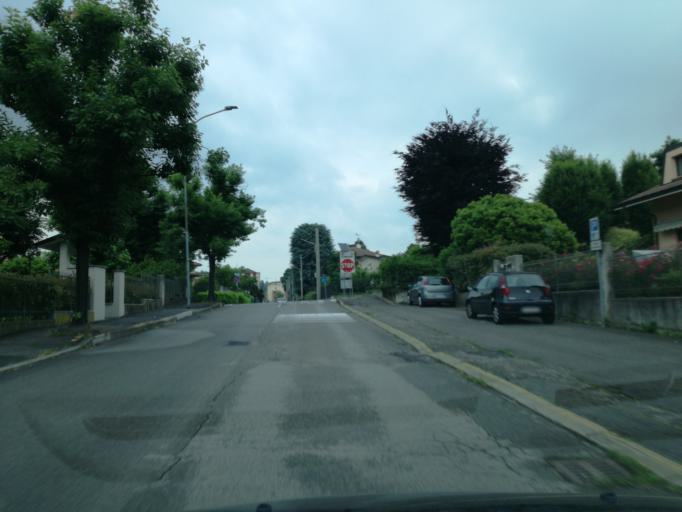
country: IT
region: Lombardy
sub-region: Provincia di Monza e Brianza
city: Carnate
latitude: 45.6498
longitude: 9.3754
